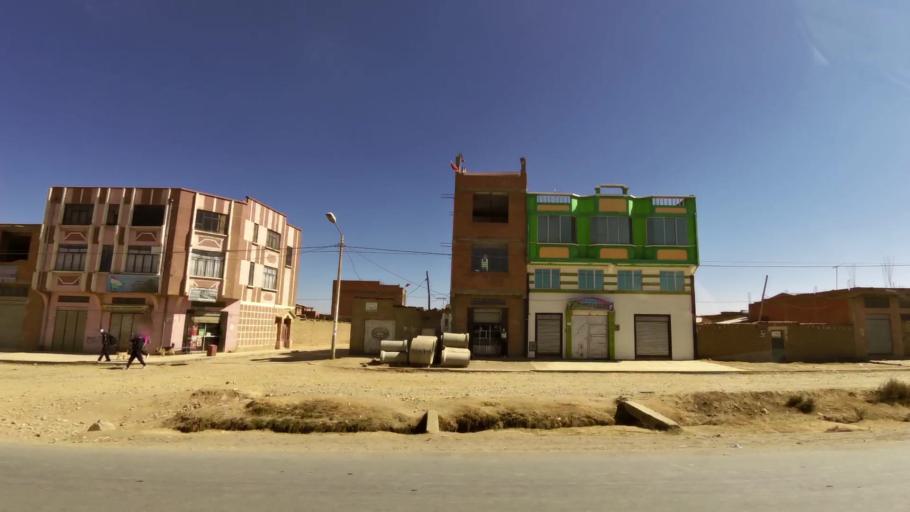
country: BO
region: La Paz
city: La Paz
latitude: -16.5644
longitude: -68.2184
